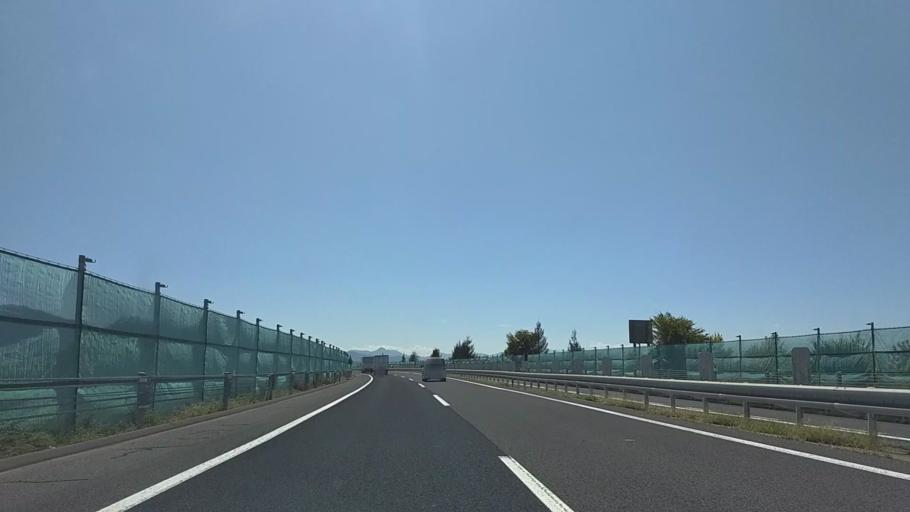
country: JP
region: Nagano
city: Suzaka
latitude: 36.6721
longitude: 138.2864
